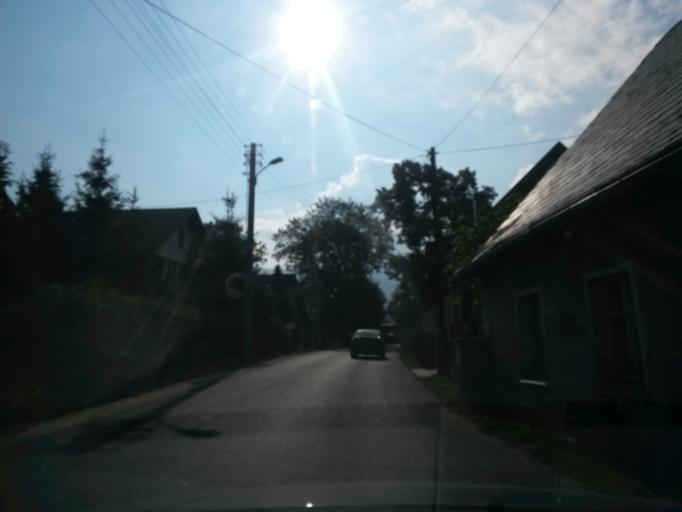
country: PL
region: Lower Silesian Voivodeship
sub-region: Powiat jeleniogorski
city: Karpacz
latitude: 50.7968
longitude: 15.7773
